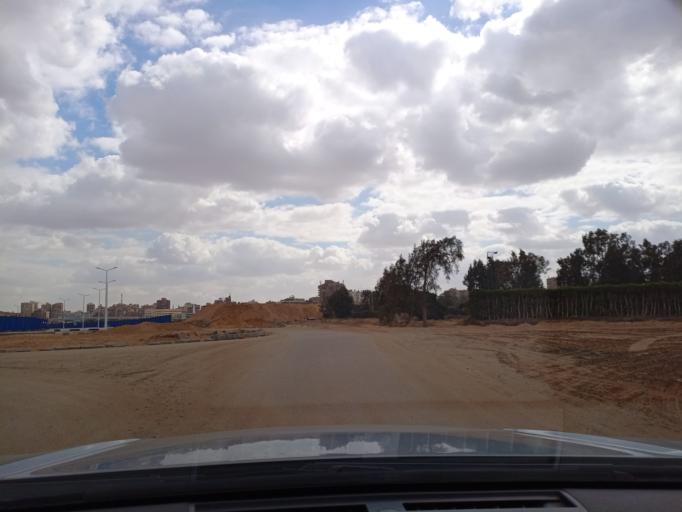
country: EG
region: Muhafazat al Qalyubiyah
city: Al Khankah
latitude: 30.1243
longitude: 31.3512
